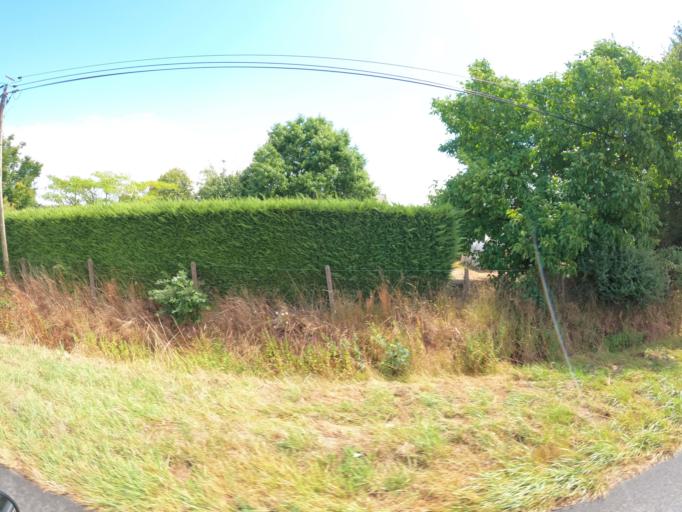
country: FR
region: Pays de la Loire
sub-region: Departement de Maine-et-Loire
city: Feneu
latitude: 47.5866
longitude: -0.5905
